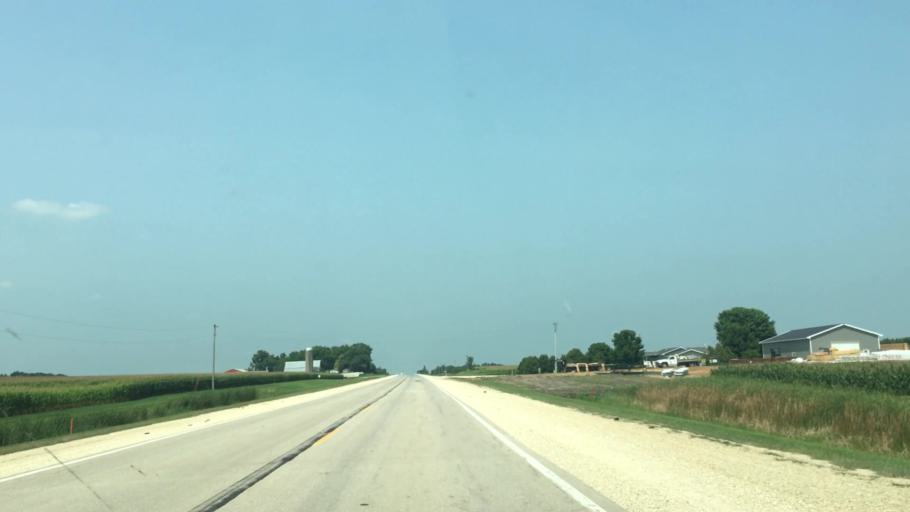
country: US
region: Iowa
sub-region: Fayette County
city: Fayette
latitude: 42.7654
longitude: -91.8045
